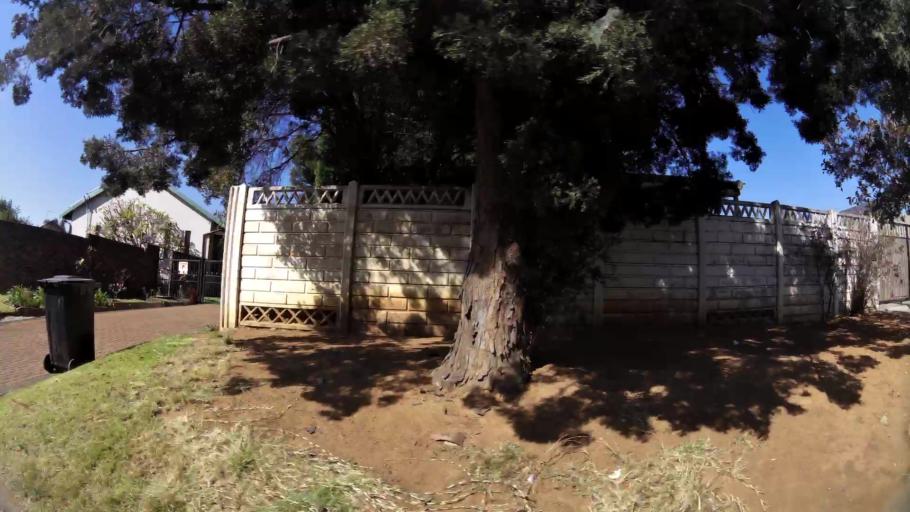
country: ZA
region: Gauteng
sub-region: Ekurhuleni Metropolitan Municipality
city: Tembisa
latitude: -26.0492
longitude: 28.2307
